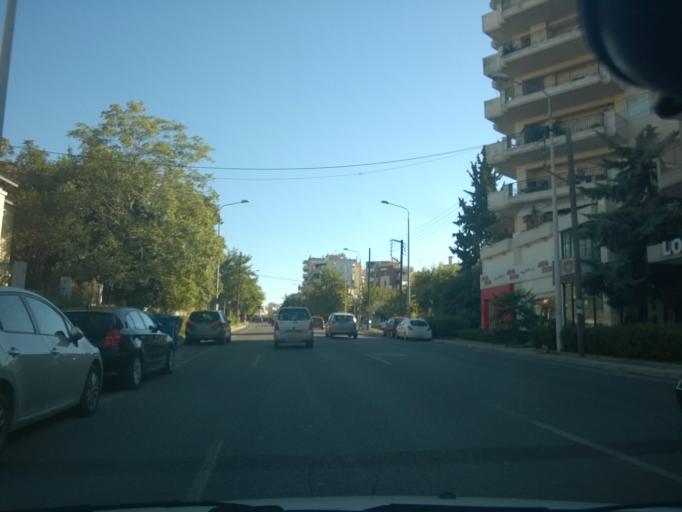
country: GR
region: Central Macedonia
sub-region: Nomos Thessalonikis
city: Kalamaria
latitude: 40.5939
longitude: 22.9539
